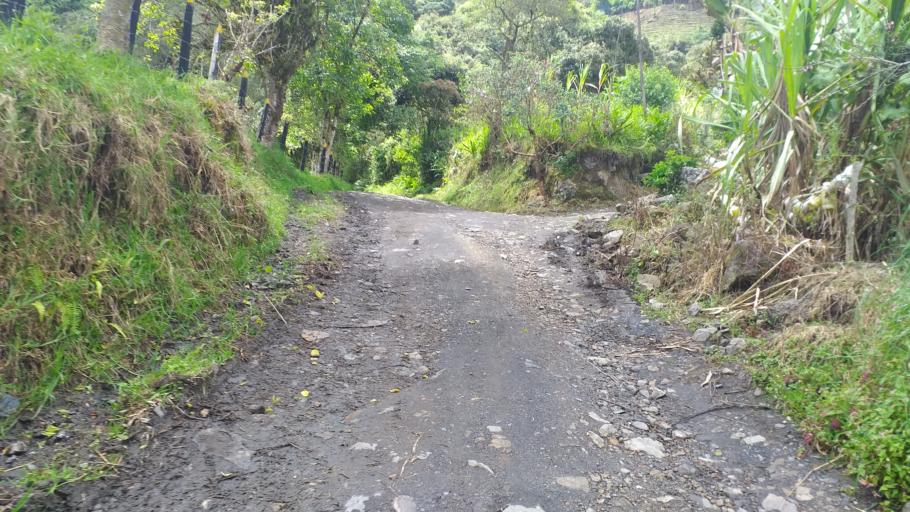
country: CO
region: Cundinamarca
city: Tenza
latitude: 5.1231
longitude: -73.4571
